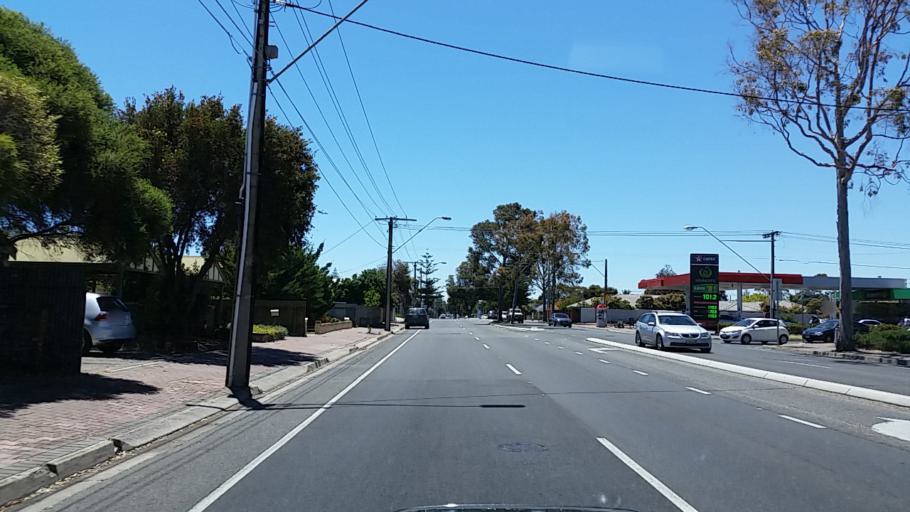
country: AU
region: South Australia
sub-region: Holdfast Bay
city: North Brighton
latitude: -34.9921
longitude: 138.5210
